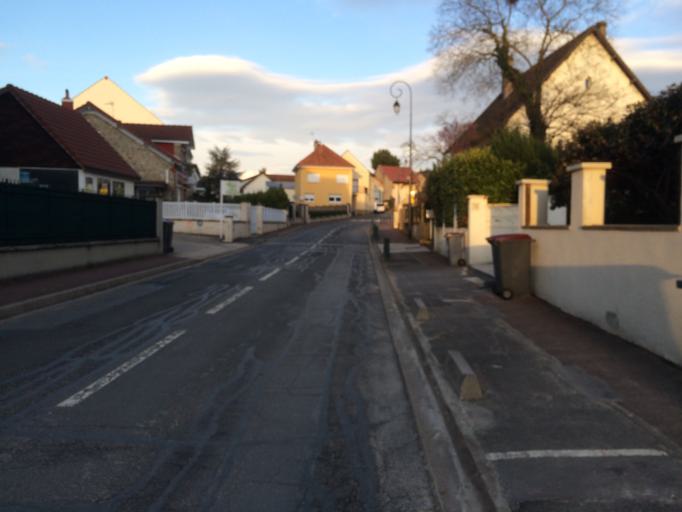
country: FR
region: Ile-de-France
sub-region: Departement de l'Essonne
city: Villebon-sur-Yvette
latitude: 48.6993
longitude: 2.2402
